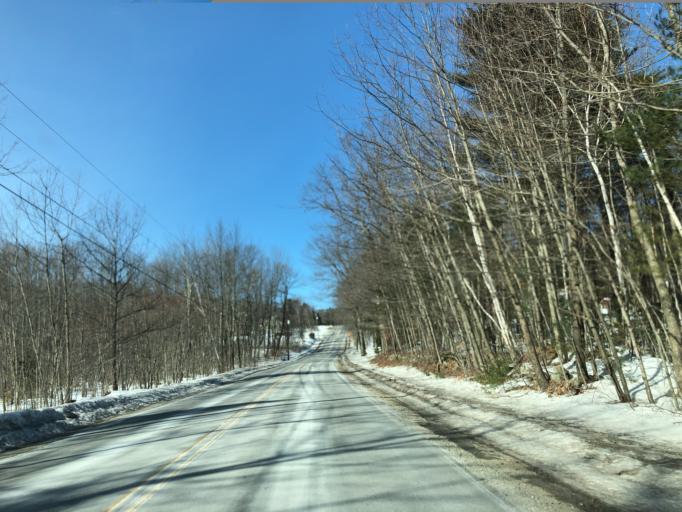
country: US
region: Maine
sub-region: Androscoggin County
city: Minot
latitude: 44.1292
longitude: -70.3028
